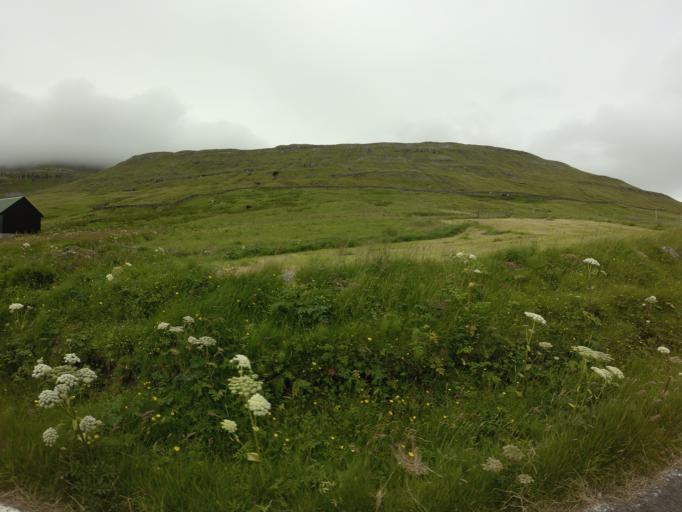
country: FO
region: Sandoy
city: Sandur
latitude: 61.8110
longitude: -6.6880
